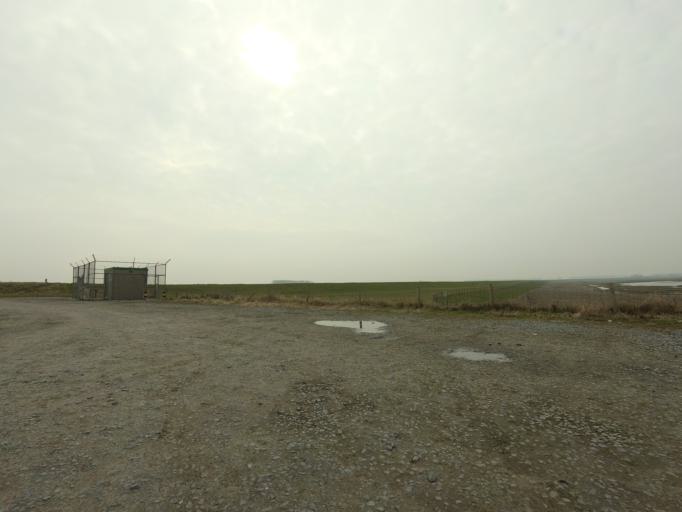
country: BE
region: Flanders
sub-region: Provincie Oost-Vlaanderen
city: Sint-Gillis-Waas
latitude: 51.3327
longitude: 4.1838
